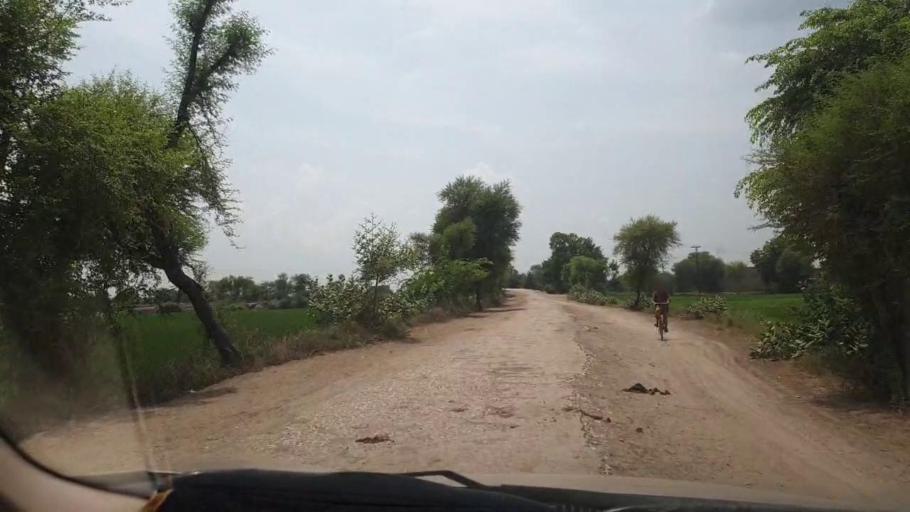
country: PK
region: Sindh
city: Larkana
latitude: 27.6054
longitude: 68.1255
